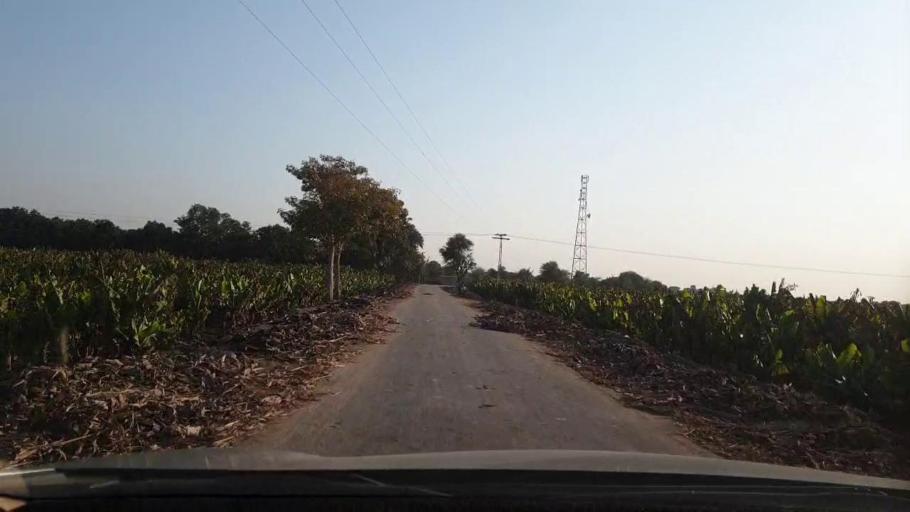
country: PK
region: Sindh
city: Berani
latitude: 25.6411
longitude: 68.8084
